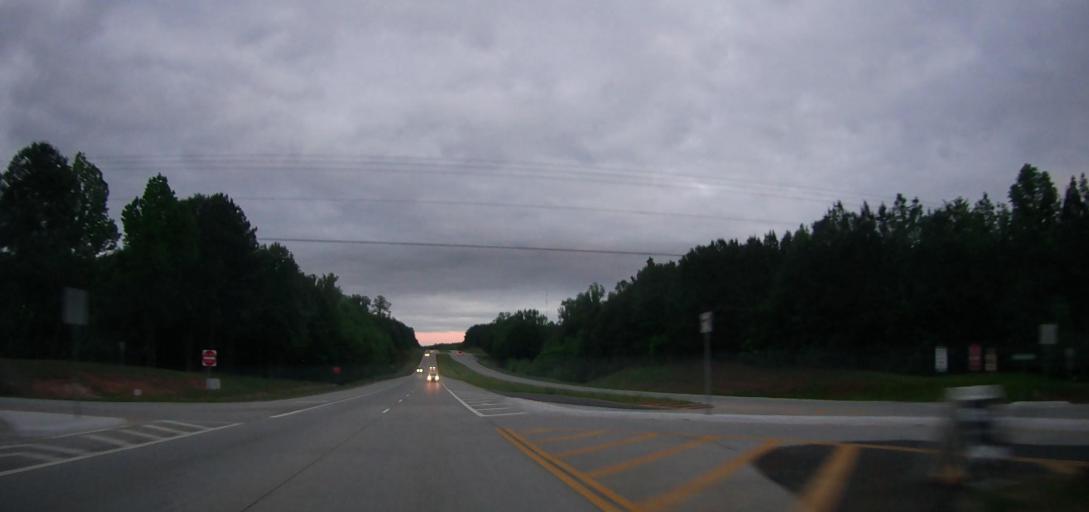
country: US
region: Georgia
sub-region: Jackson County
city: Jefferson
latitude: 34.1129
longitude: -83.5986
